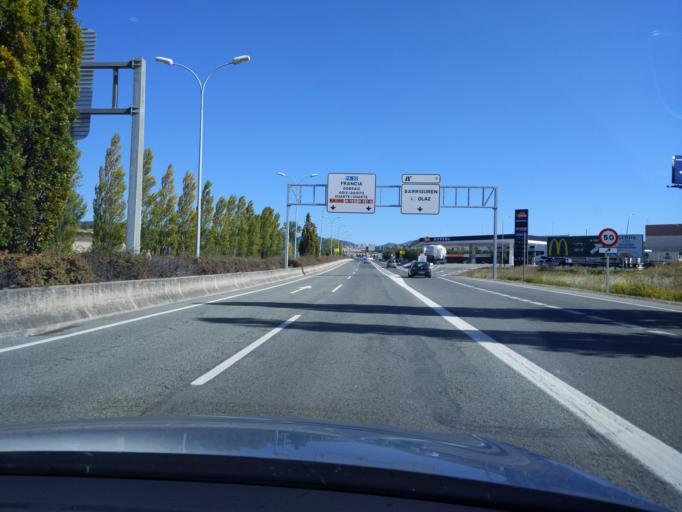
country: ES
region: Navarre
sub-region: Provincia de Navarra
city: Egues-Uharte
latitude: 42.8158
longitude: -1.5956
